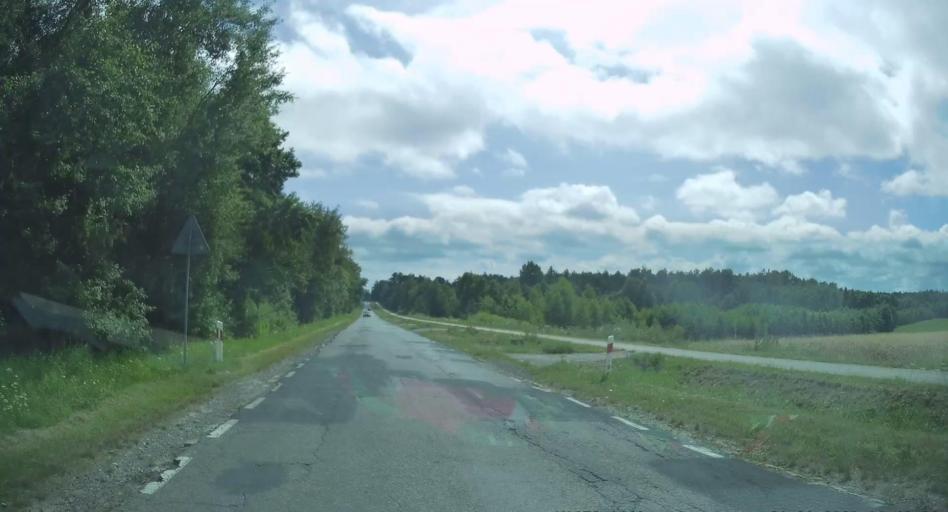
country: PL
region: Swietokrzyskie
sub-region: Powiat opatowski
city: Iwaniska
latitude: 50.7032
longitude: 21.3292
